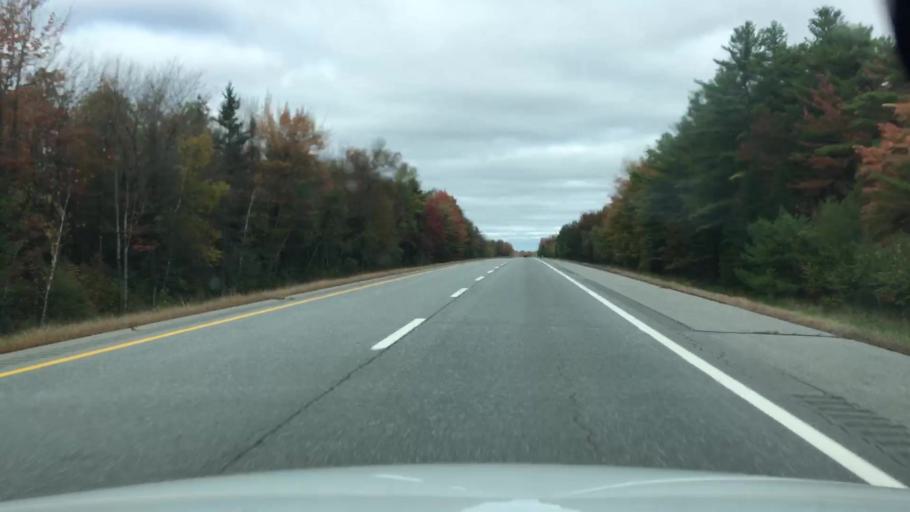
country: US
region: Maine
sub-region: Kennebec County
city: Clinton
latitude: 44.6730
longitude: -69.4848
